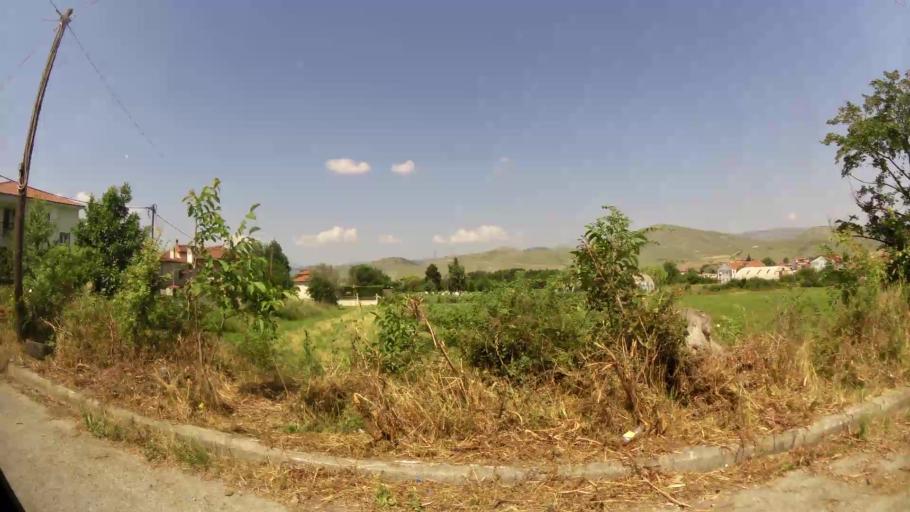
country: GR
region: West Macedonia
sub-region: Nomos Kozanis
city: Koila
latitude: 40.3271
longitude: 21.7915
